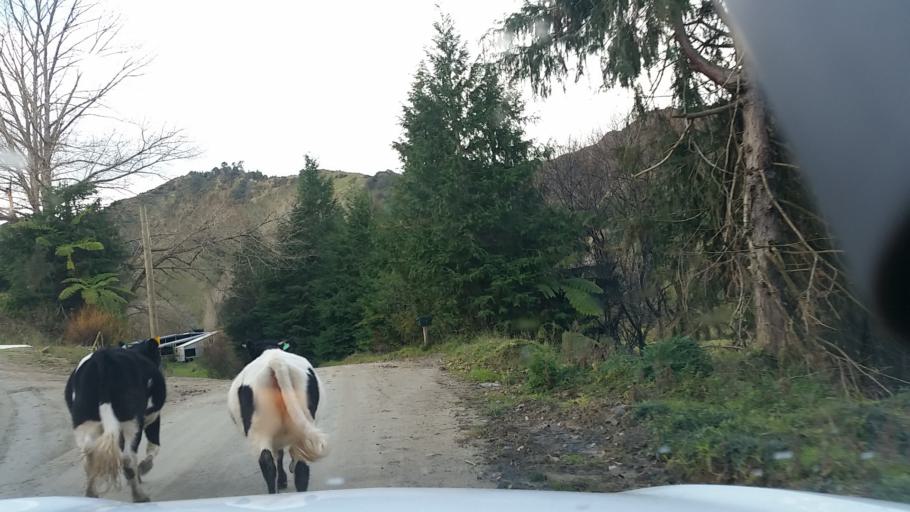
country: NZ
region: Taranaki
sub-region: South Taranaki District
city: Patea
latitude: -39.5617
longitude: 174.8046
